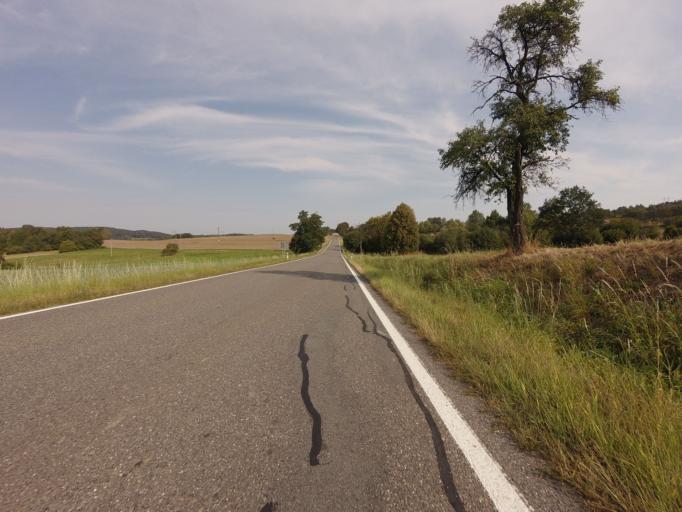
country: CZ
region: Central Bohemia
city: Petrovice
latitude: 49.5138
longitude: 14.3591
